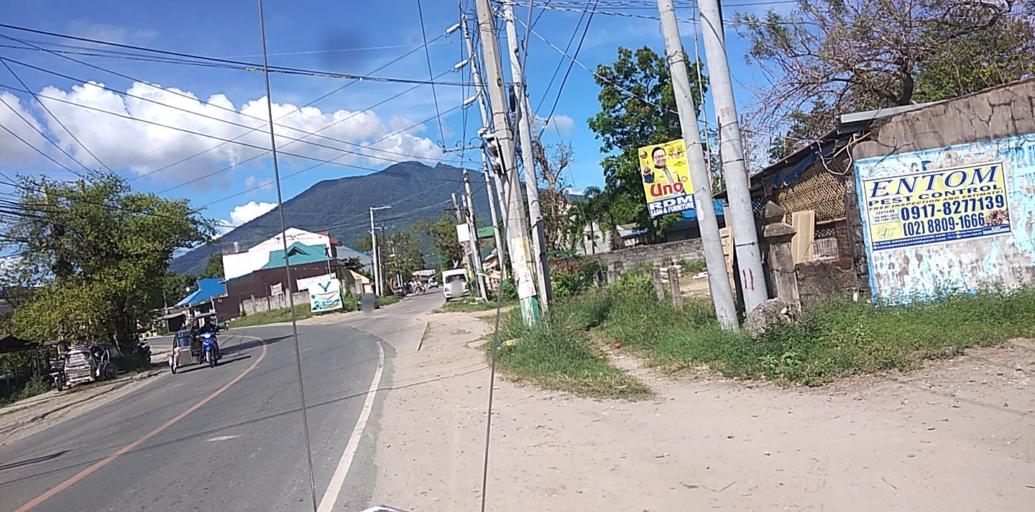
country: PH
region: Central Luzon
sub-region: Province of Pampanga
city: Arayat
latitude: 15.1432
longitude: 120.7714
